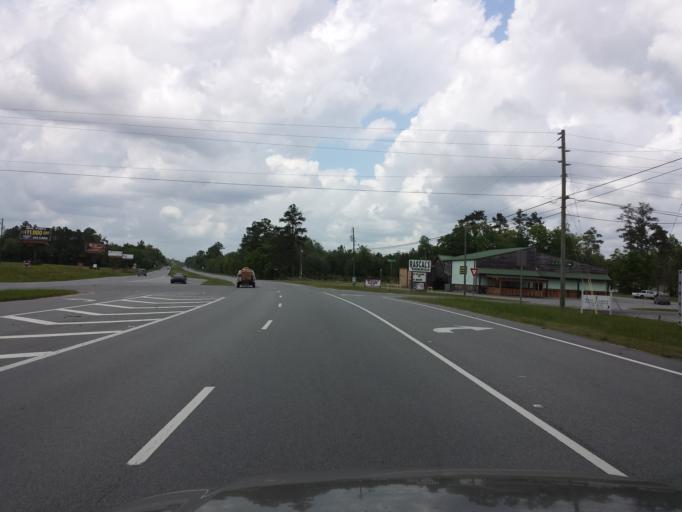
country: US
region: Georgia
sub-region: Lowndes County
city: Valdosta
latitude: 30.7008
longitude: -83.2106
